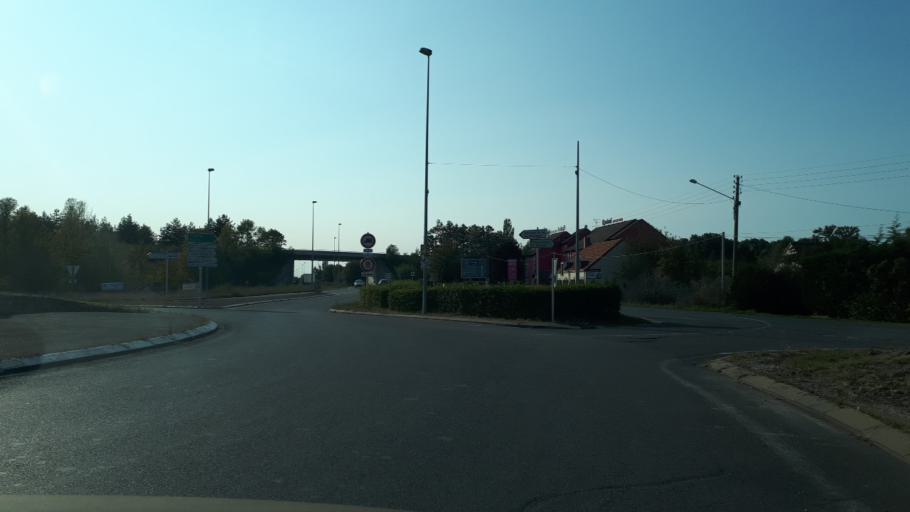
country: FR
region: Centre
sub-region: Departement du Cher
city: Vierzon
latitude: 47.2145
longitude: 2.1168
